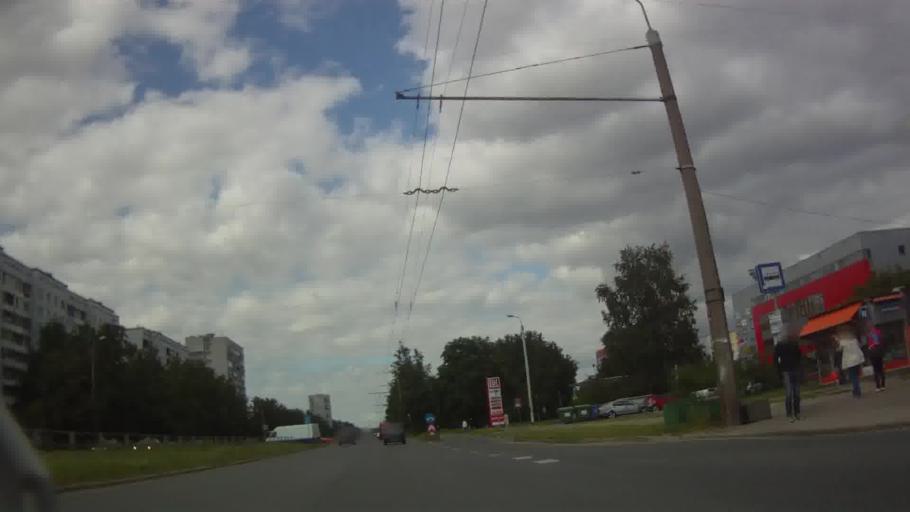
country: LV
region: Stopini
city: Ulbroka
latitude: 56.9342
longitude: 24.2019
